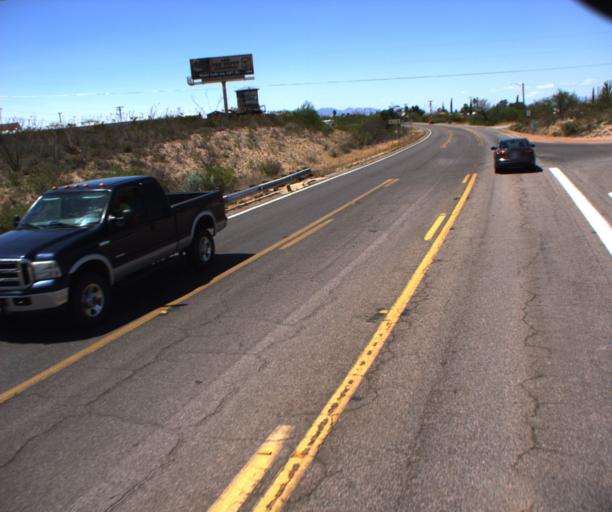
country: US
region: Arizona
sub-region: Cochise County
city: Tombstone
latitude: 31.7095
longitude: -110.0562
